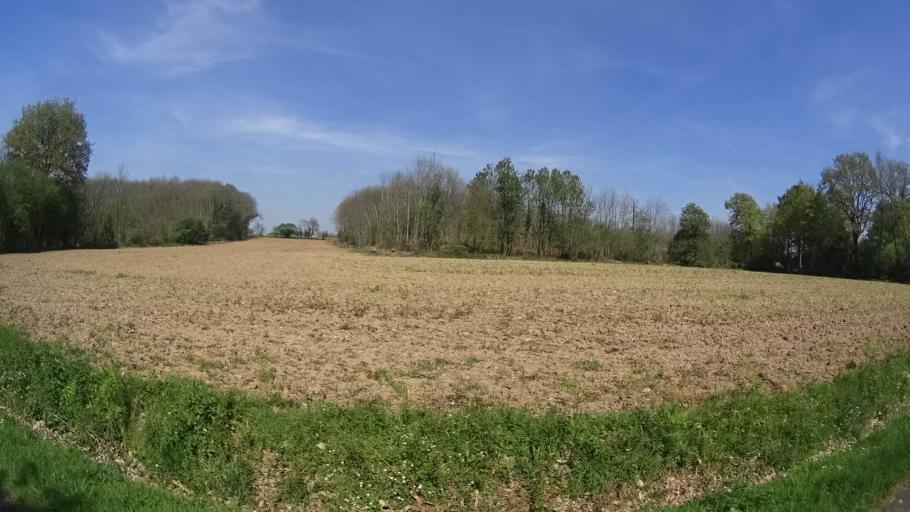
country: FR
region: Pays de la Loire
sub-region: Departement de la Loire-Atlantique
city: Fegreac
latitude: 47.5950
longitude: -2.0572
